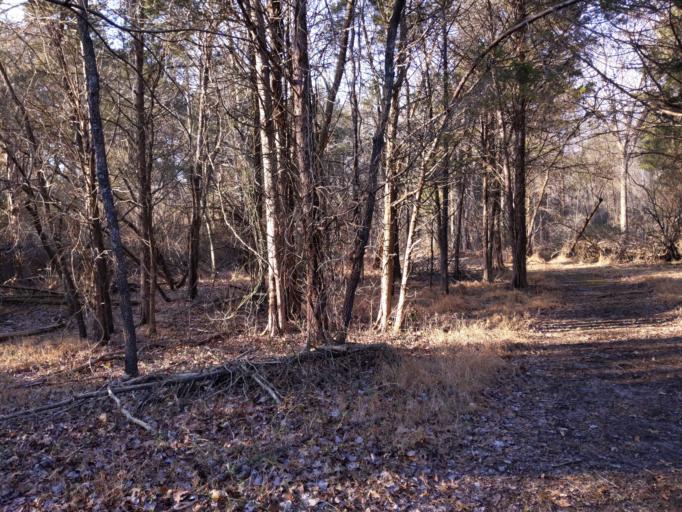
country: US
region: Virginia
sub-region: Loudoun County
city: Dulles Town Center
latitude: 39.0180
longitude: -77.3982
